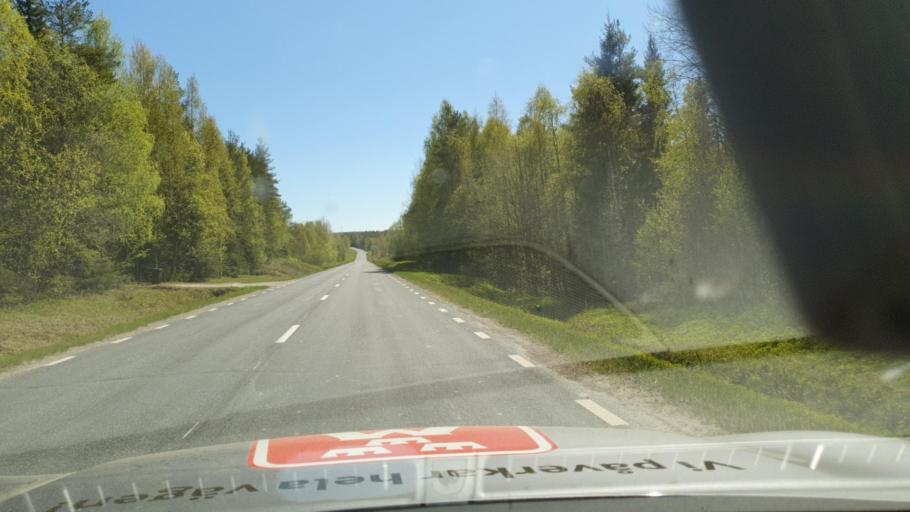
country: SE
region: Vaesternorrland
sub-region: OErnskoeldsviks Kommun
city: Ornskoldsvik
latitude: 63.5758
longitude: 18.5493
